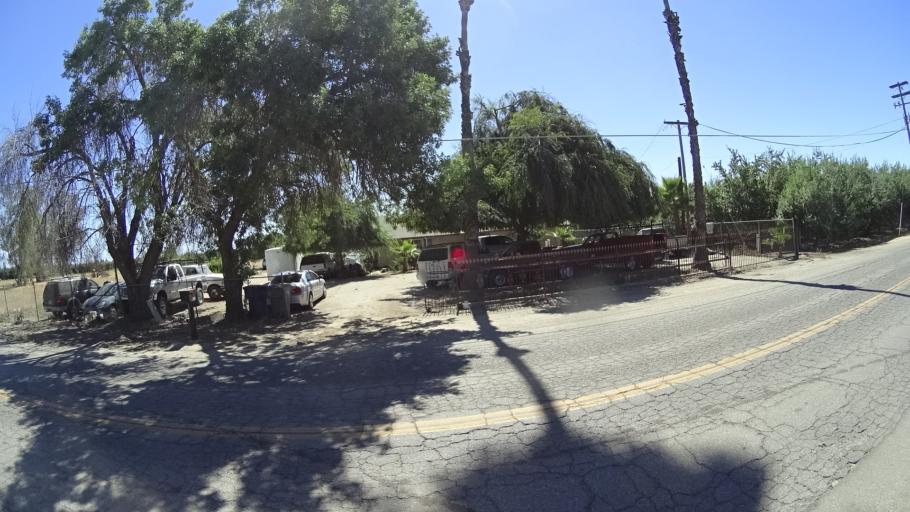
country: US
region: California
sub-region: Fresno County
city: West Park
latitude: 36.6946
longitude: -119.8089
